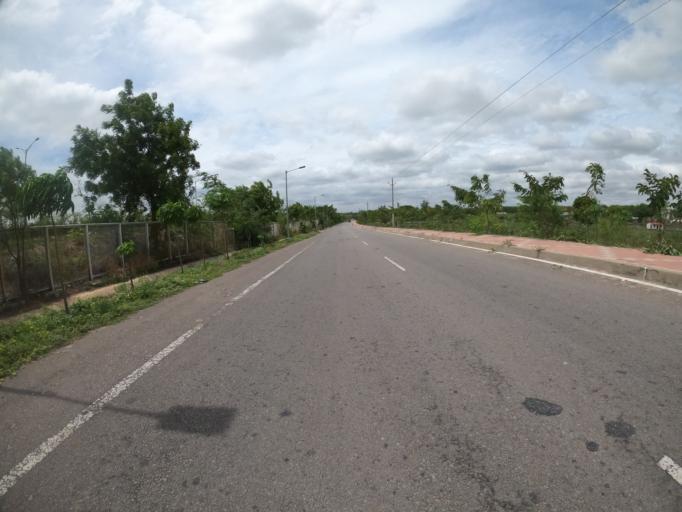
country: IN
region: Telangana
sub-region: Rangareddi
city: Balapur
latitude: 17.2873
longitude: 78.3819
